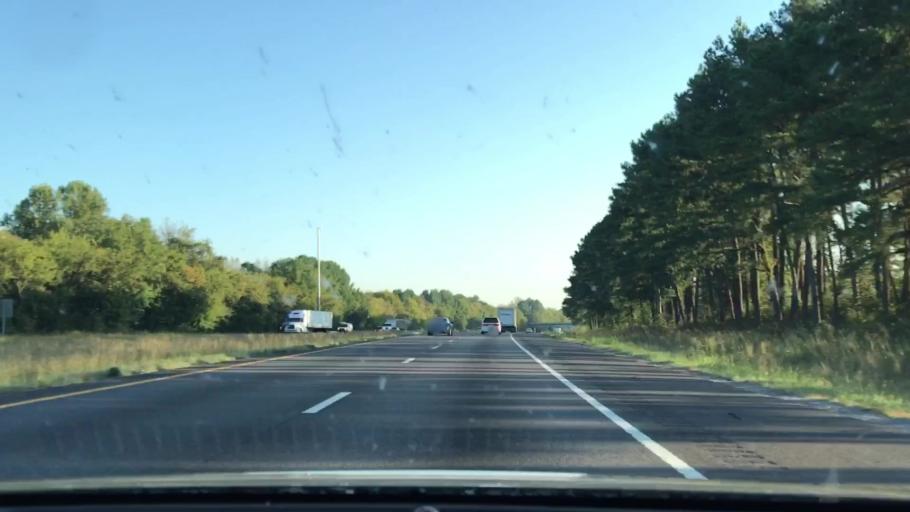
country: US
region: Tennessee
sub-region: Sumner County
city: White House
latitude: 36.4950
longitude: -86.6701
